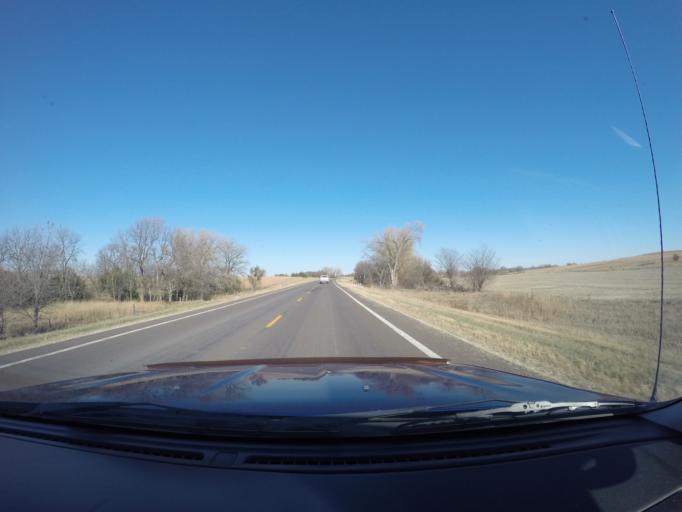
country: US
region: Kansas
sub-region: Marshall County
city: Blue Rapids
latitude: 39.5059
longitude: -96.7549
